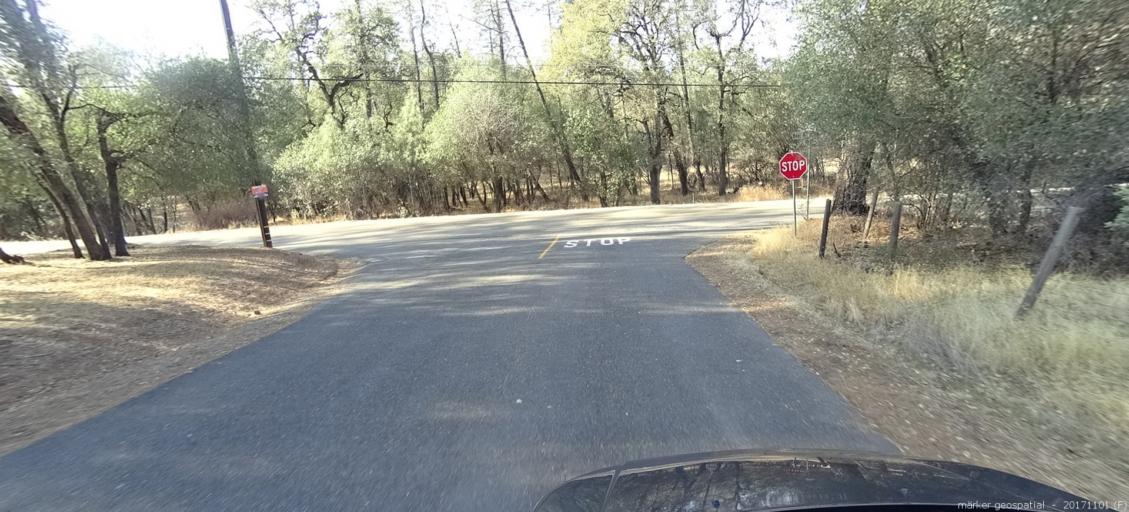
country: US
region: California
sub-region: Shasta County
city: Shasta Lake
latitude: 40.6808
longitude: -122.2983
